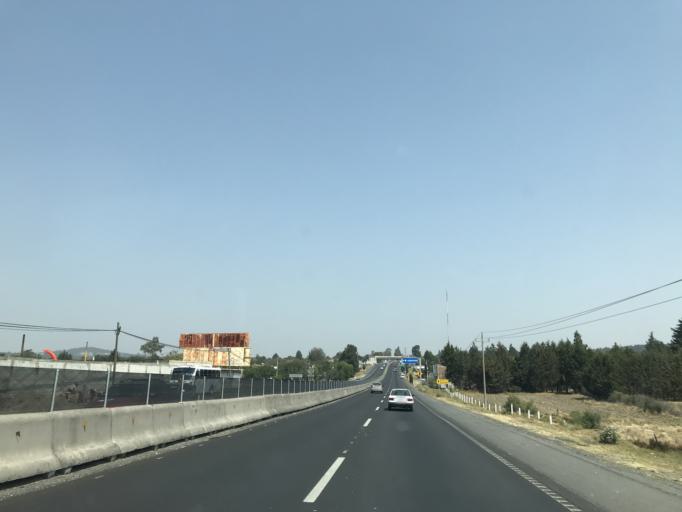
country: MX
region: Tlaxcala
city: Yauhquemehcan
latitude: 19.3982
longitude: -98.1831
